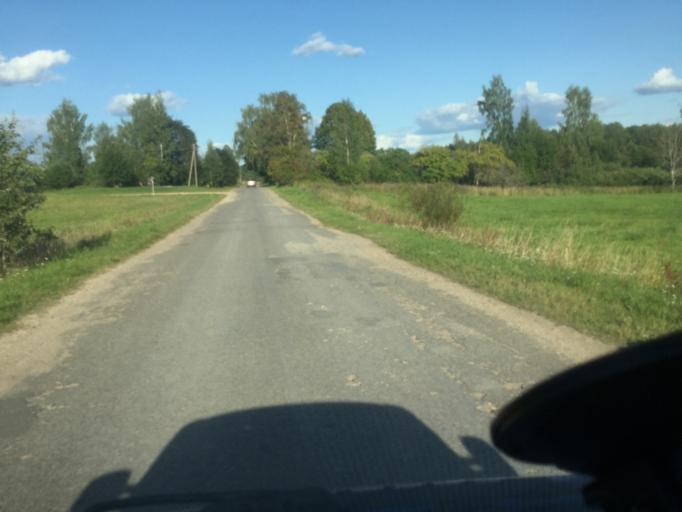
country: BY
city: Osveya
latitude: 56.0205
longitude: 28.2610
